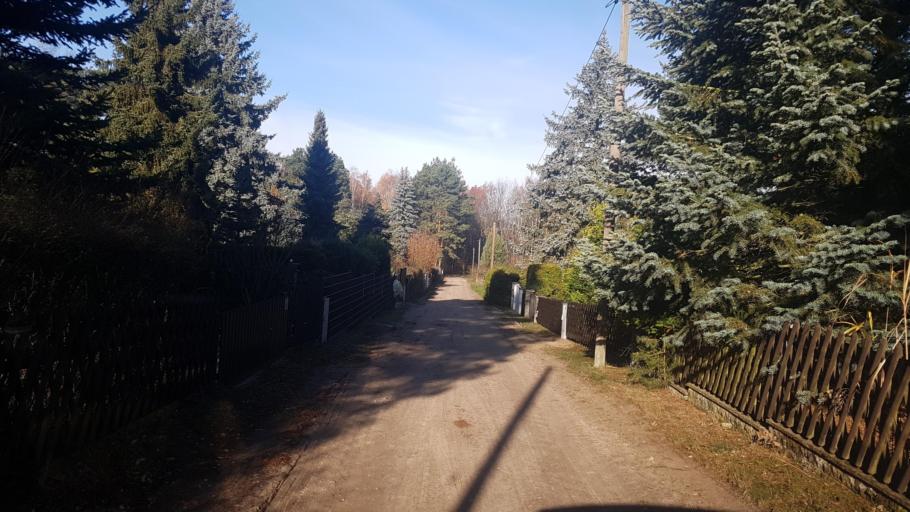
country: DE
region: Brandenburg
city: Niemegk
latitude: 52.0725
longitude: 12.7052
